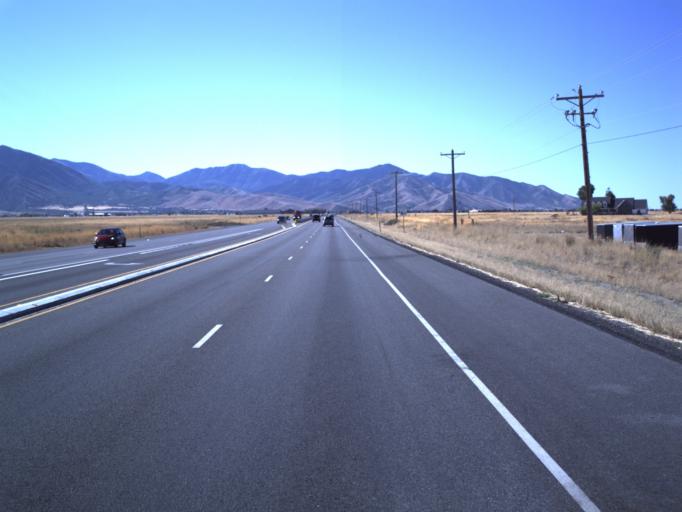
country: US
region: Utah
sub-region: Tooele County
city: Erda
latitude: 40.5930
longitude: -112.2941
